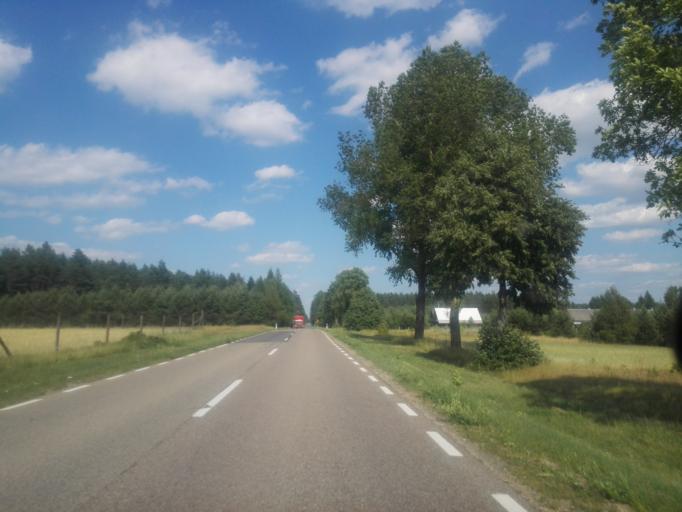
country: PL
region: Podlasie
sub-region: Powiat sejnenski
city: Krasnopol
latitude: 53.9575
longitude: 23.2205
